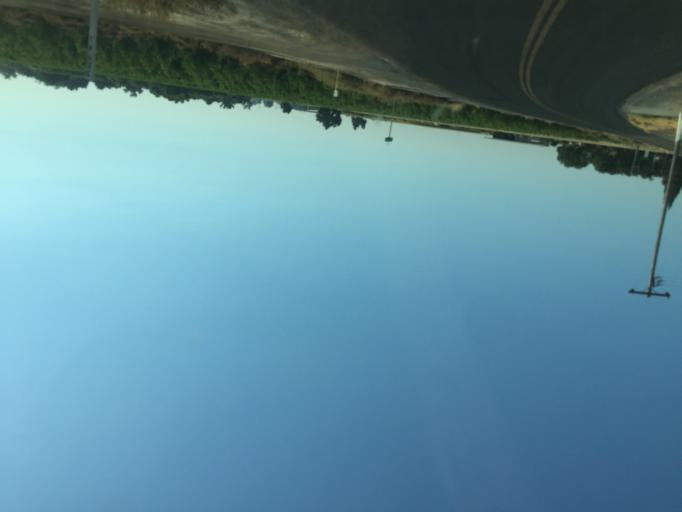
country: US
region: California
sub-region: Fresno County
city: Kingsburg
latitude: 36.4882
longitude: -119.5281
